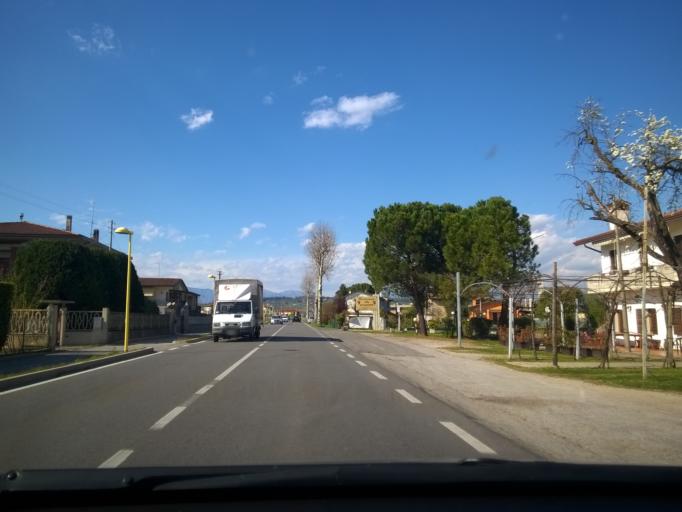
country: IT
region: Veneto
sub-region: Provincia di Treviso
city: Nervesa della Battaglia
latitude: 45.8195
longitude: 12.2238
